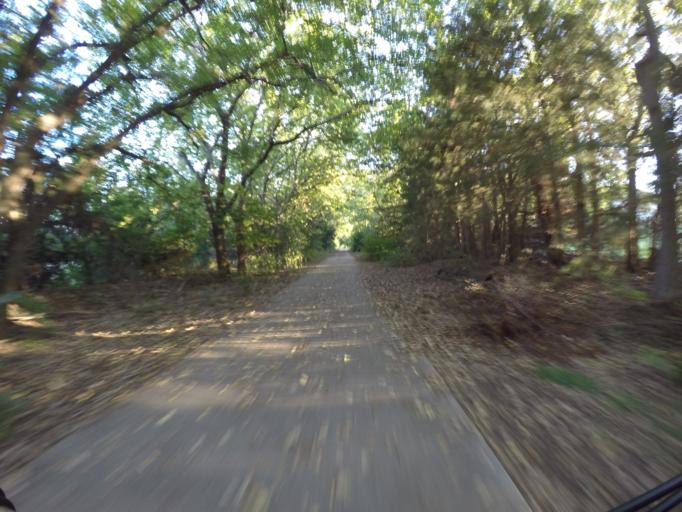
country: US
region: Kansas
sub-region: Riley County
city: Manhattan
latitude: 39.2081
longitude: -96.6261
